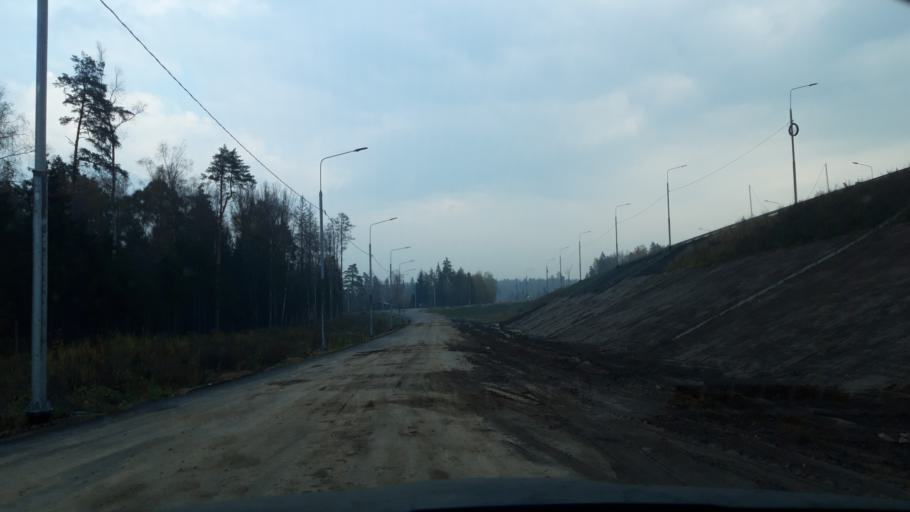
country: RU
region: Moskovskaya
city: Lozhki
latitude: 56.0439
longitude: 37.1013
